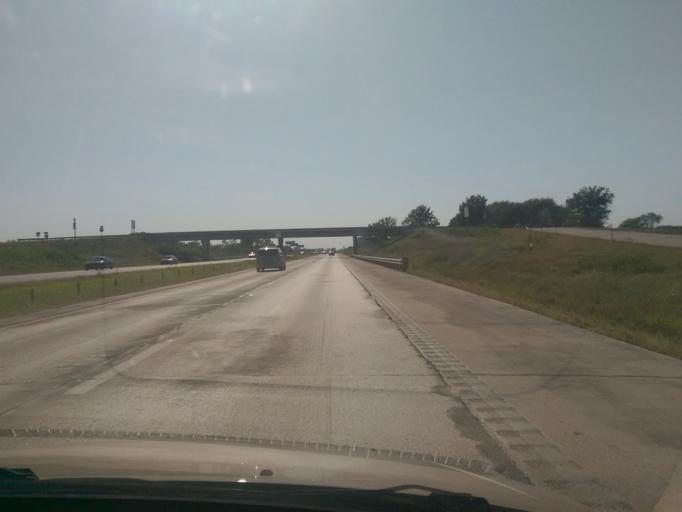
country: US
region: Missouri
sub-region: Saline County
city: Sweet Springs
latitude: 38.9736
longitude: -93.3300
